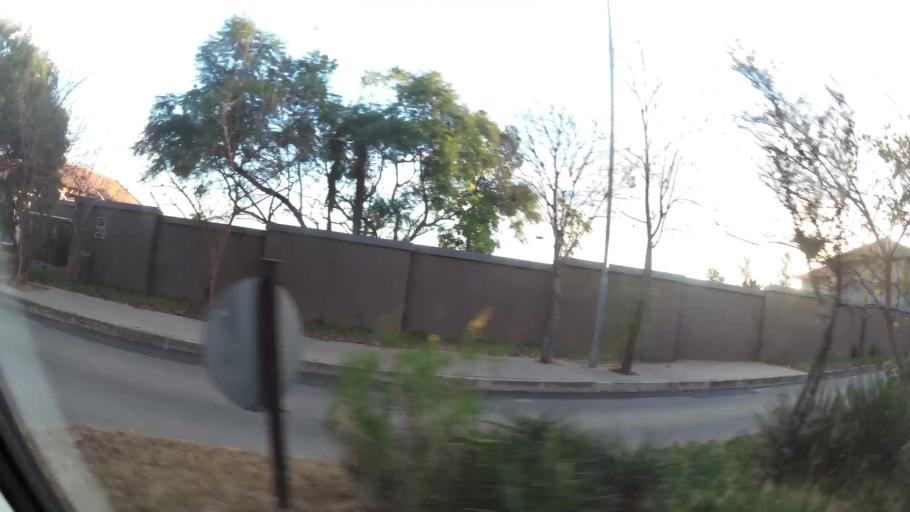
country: ZA
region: Gauteng
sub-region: City of Johannesburg Metropolitan Municipality
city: Diepsloot
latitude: -26.0145
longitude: 27.9854
